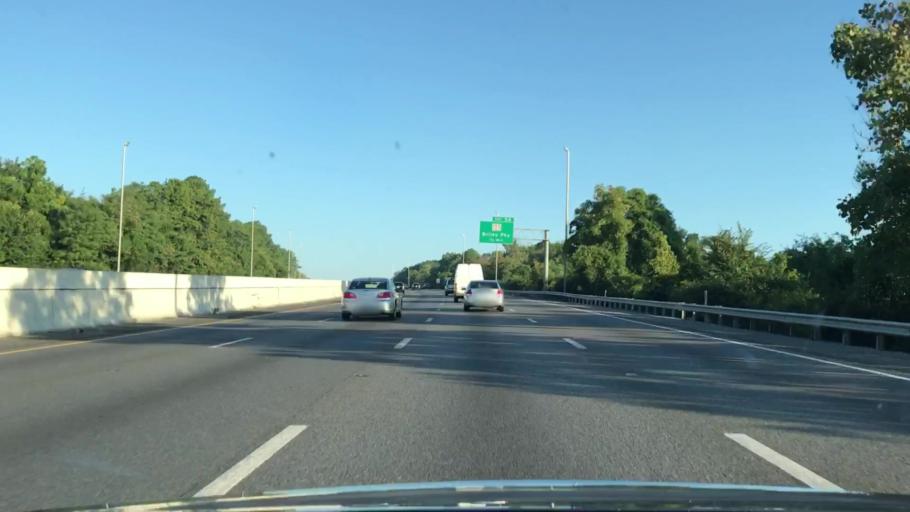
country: US
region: Tennessee
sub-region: Davidson County
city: Oak Hill
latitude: 36.1179
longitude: -86.7328
